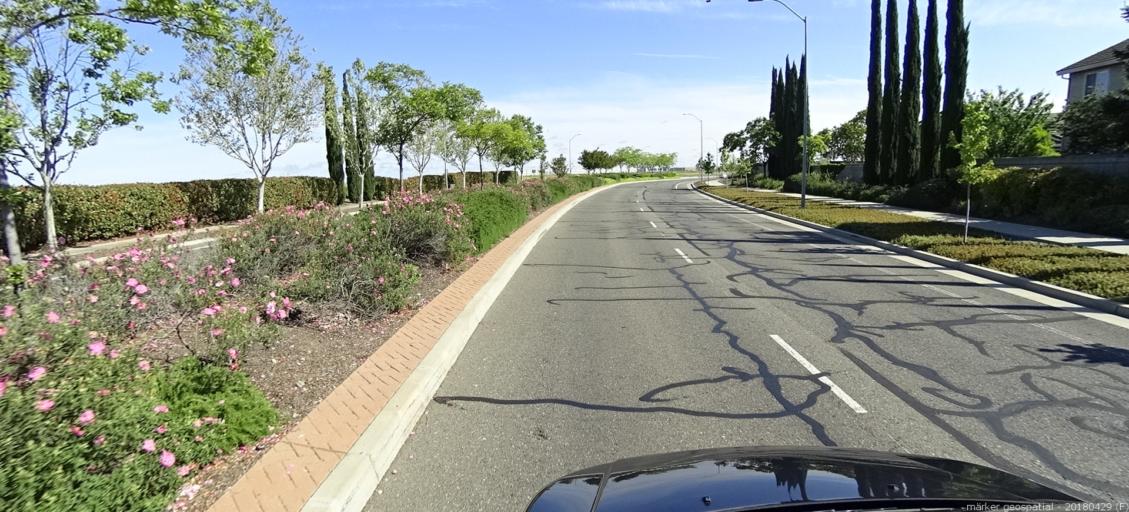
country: US
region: California
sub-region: Yolo County
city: West Sacramento
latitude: 38.5416
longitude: -121.5762
